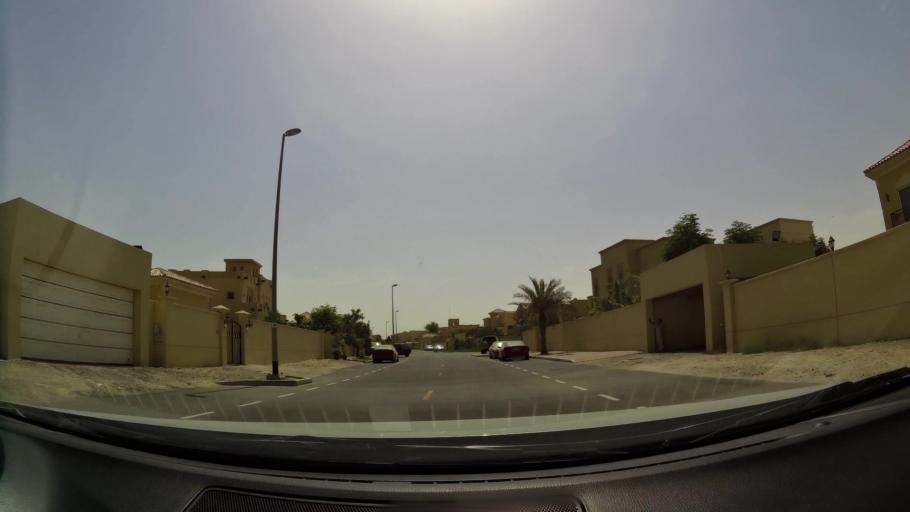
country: AE
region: Ash Shariqah
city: Sharjah
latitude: 25.1801
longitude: 55.4312
